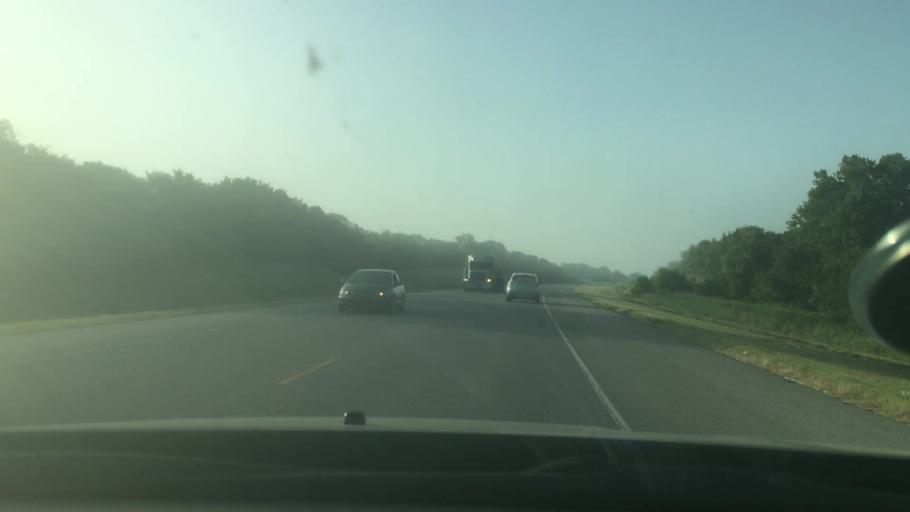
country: US
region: Oklahoma
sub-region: Pontotoc County
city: Ada
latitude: 34.7018
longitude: -96.6036
